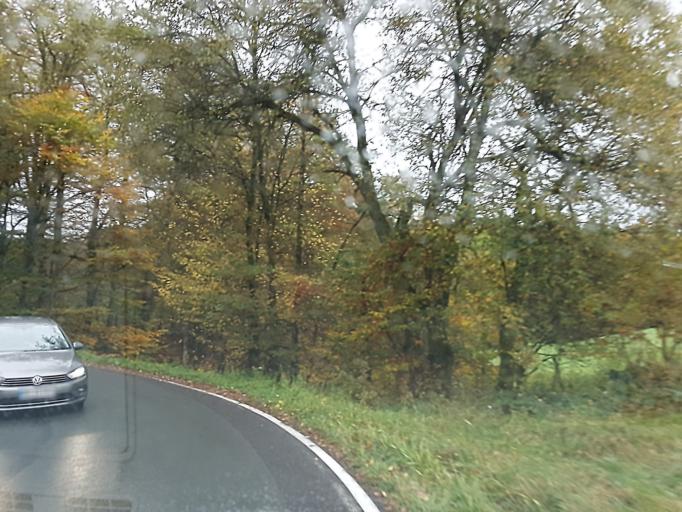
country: DE
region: North Rhine-Westphalia
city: Kierspe
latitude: 51.0914
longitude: 7.5777
